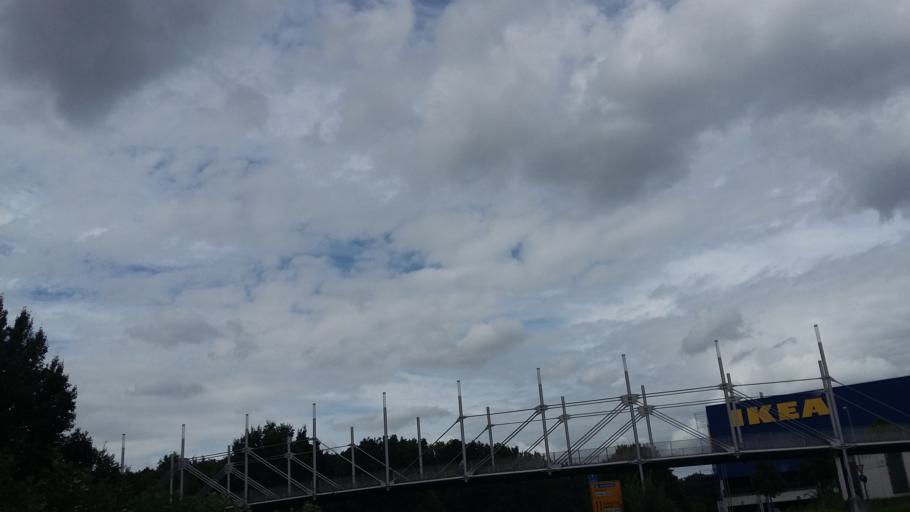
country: DE
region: Lower Saxony
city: Laatzen
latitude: 52.3115
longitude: 9.8175
